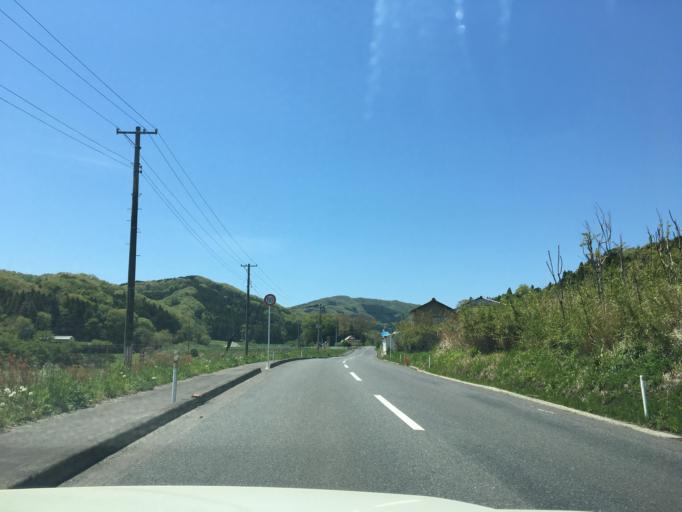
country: JP
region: Fukushima
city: Funehikimachi-funehiki
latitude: 37.3552
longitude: 140.6334
